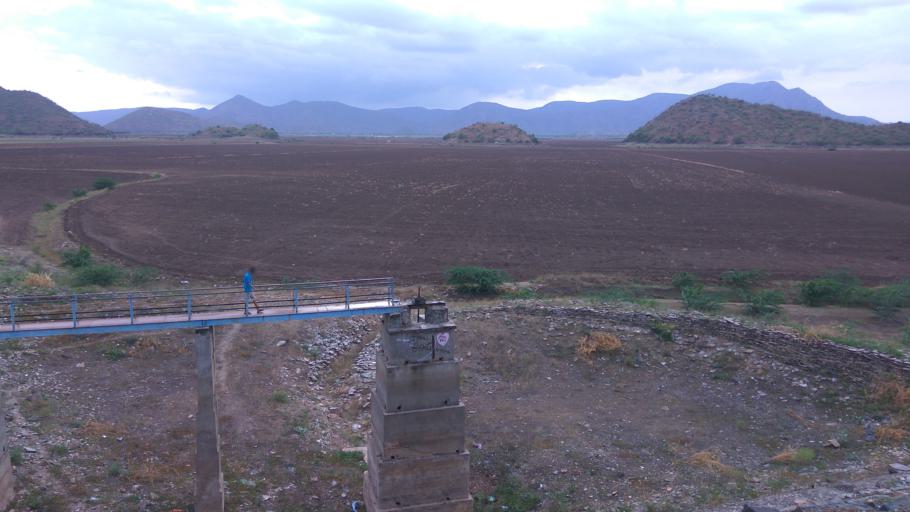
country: IN
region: Andhra Pradesh
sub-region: Prakasam
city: Cumbum
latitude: 15.5757
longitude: 79.0812
